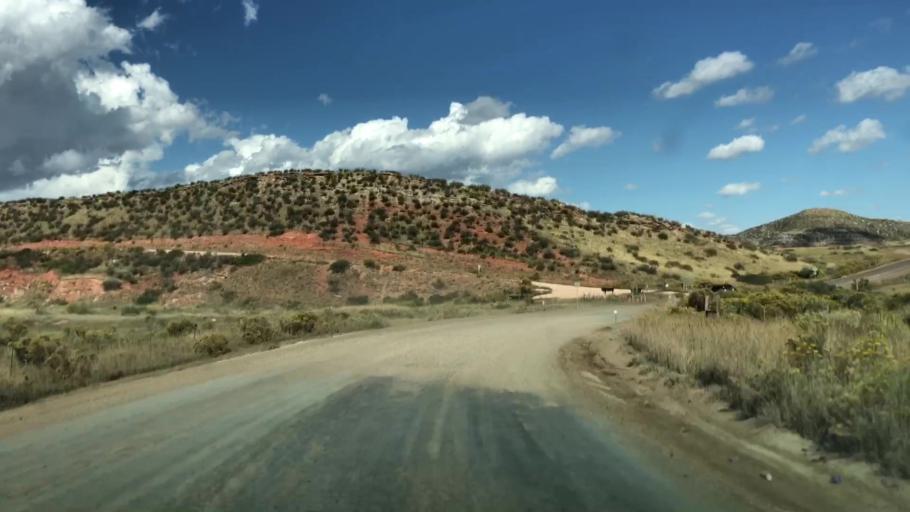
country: US
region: Colorado
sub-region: Larimer County
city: Laporte
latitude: 40.7654
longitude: -105.1732
